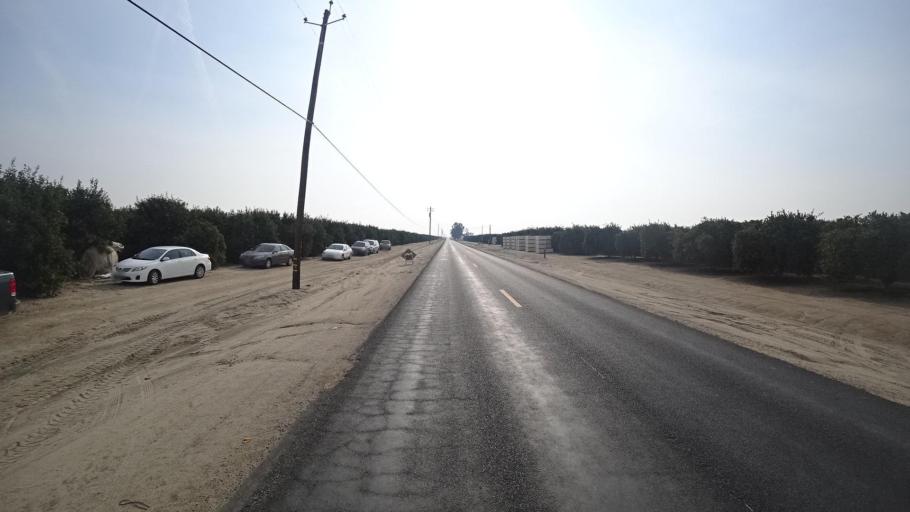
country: US
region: California
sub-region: Kern County
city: Arvin
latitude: 35.1476
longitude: -118.8508
